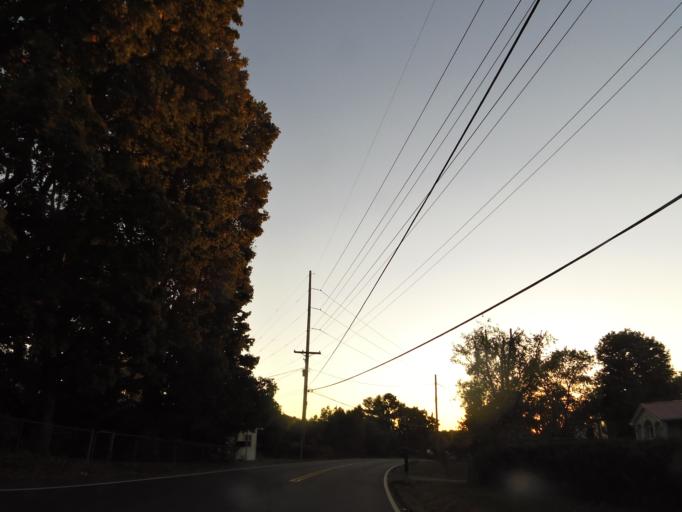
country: US
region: Tennessee
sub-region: Union County
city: Condon
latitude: 36.1242
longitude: -83.8418
